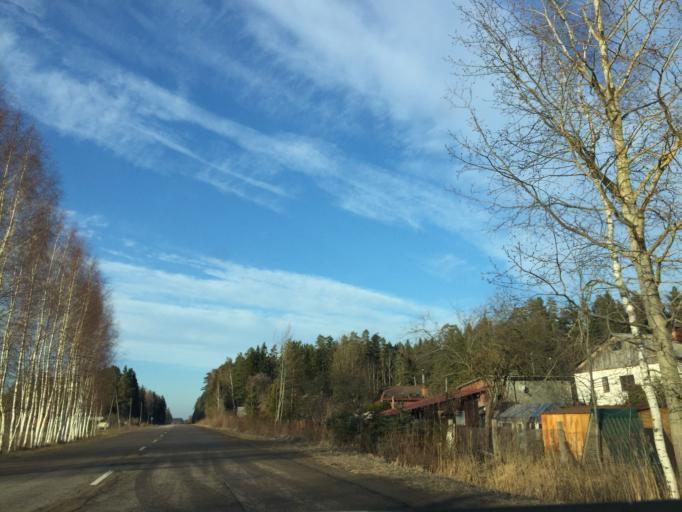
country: LV
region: Lecava
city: Iecava
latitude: 56.7168
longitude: 24.1118
